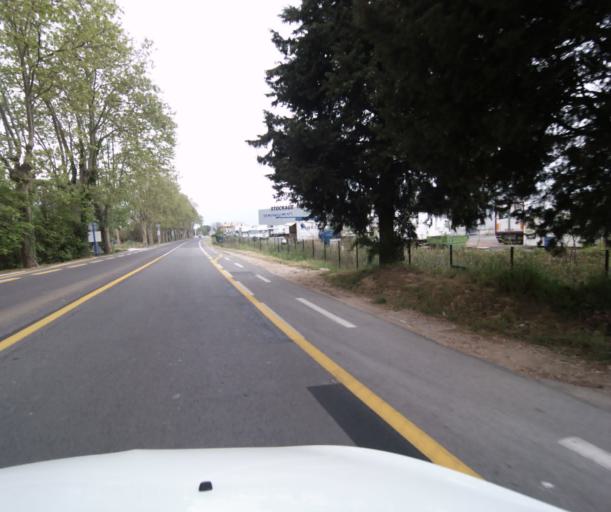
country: FR
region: Provence-Alpes-Cote d'Azur
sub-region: Departement du Var
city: La Crau
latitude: 43.1295
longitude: 6.0733
